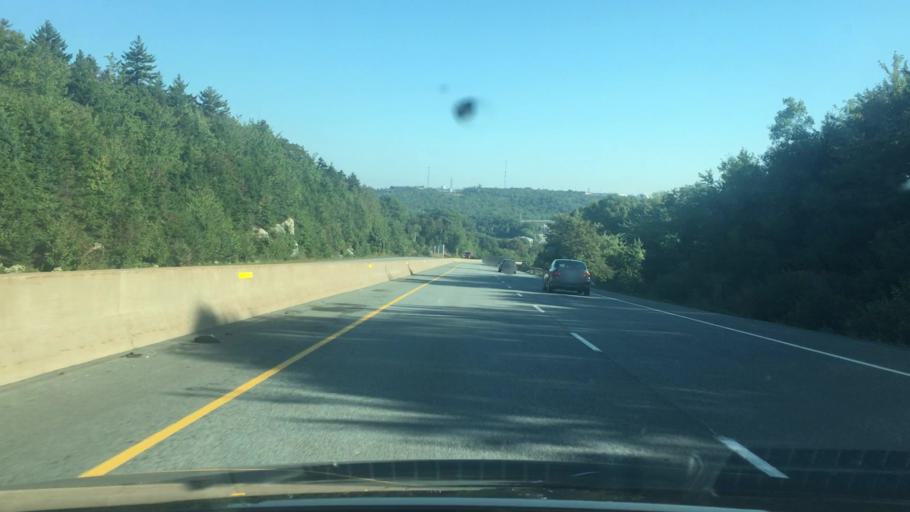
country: CA
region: Nova Scotia
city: Dartmouth
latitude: 44.7372
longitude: -63.6617
